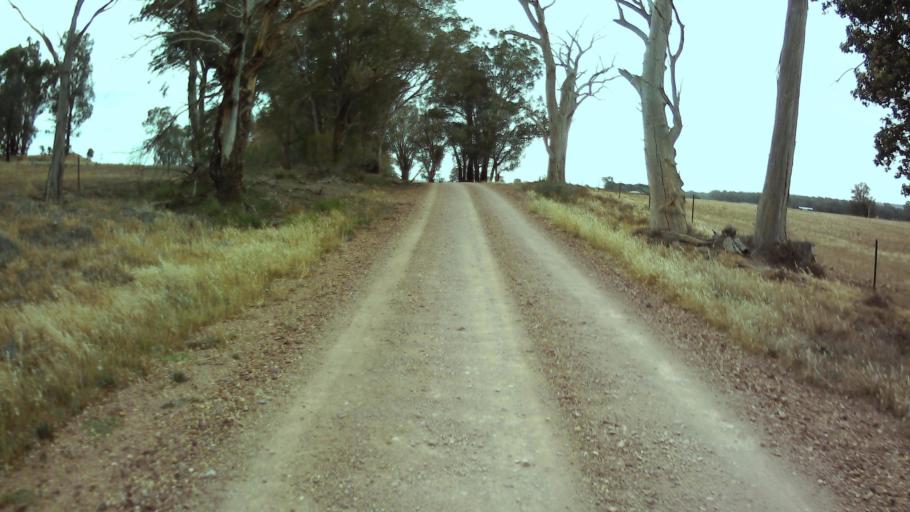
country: AU
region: New South Wales
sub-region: Weddin
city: Grenfell
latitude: -33.9137
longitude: 148.2887
